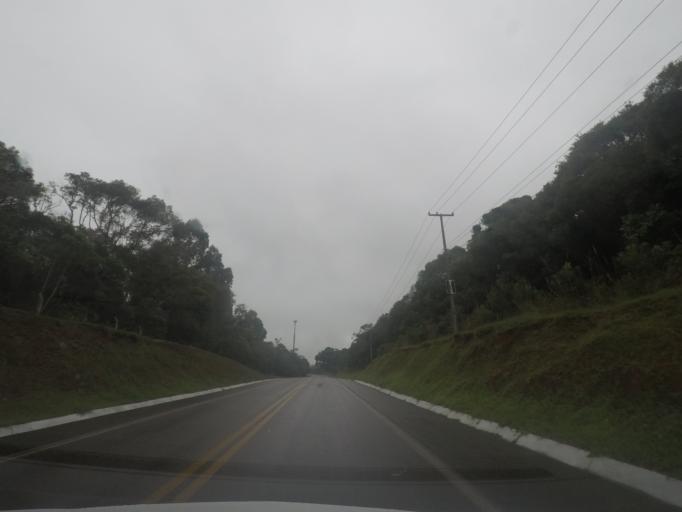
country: BR
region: Parana
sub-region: Colombo
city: Colombo
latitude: -25.3142
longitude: -49.1565
